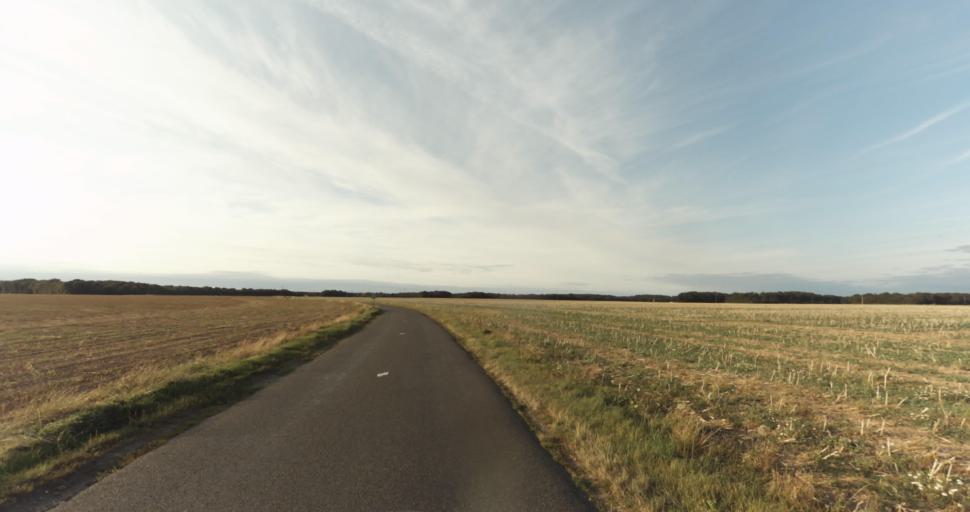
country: FR
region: Haute-Normandie
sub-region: Departement de l'Eure
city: Marcilly-sur-Eure
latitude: 48.8213
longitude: 1.2902
